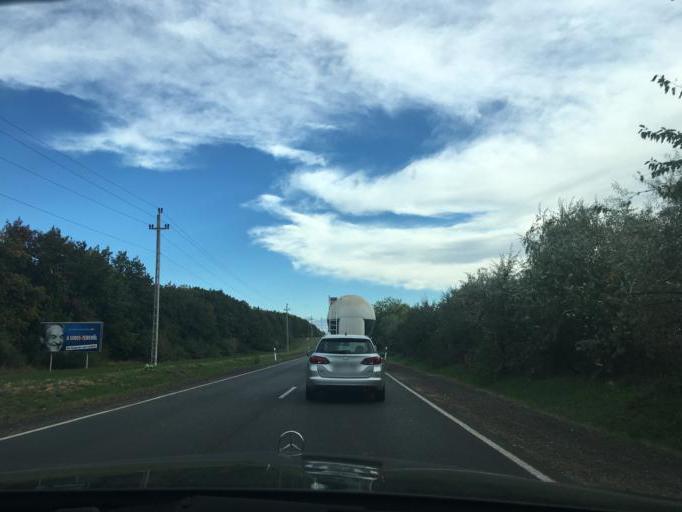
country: HU
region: Borsod-Abauj-Zemplen
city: Arnot
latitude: 48.1242
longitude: 20.8700
